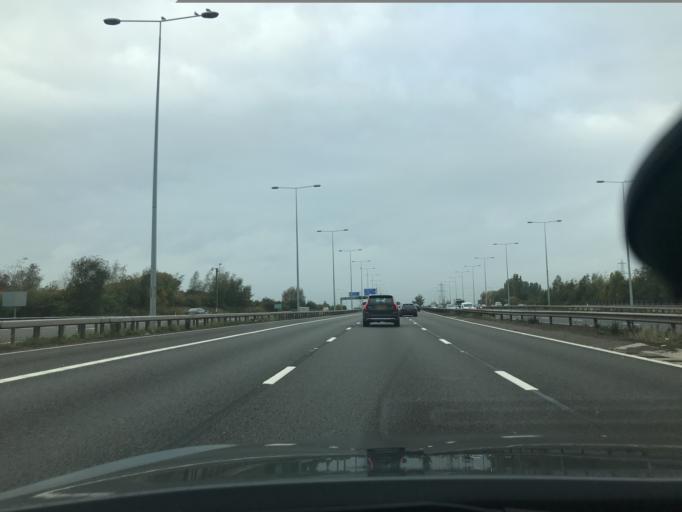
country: GB
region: England
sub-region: Trafford
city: Sale
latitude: 53.4324
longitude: -2.3064
